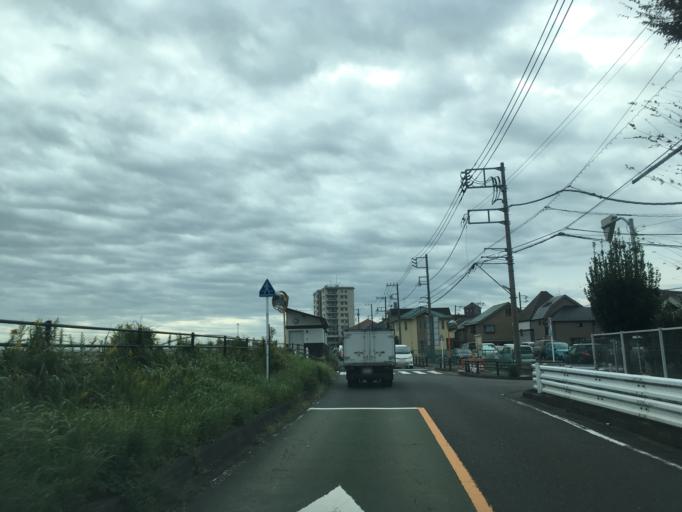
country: JP
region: Tokyo
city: Chofugaoka
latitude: 35.6443
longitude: 139.5214
